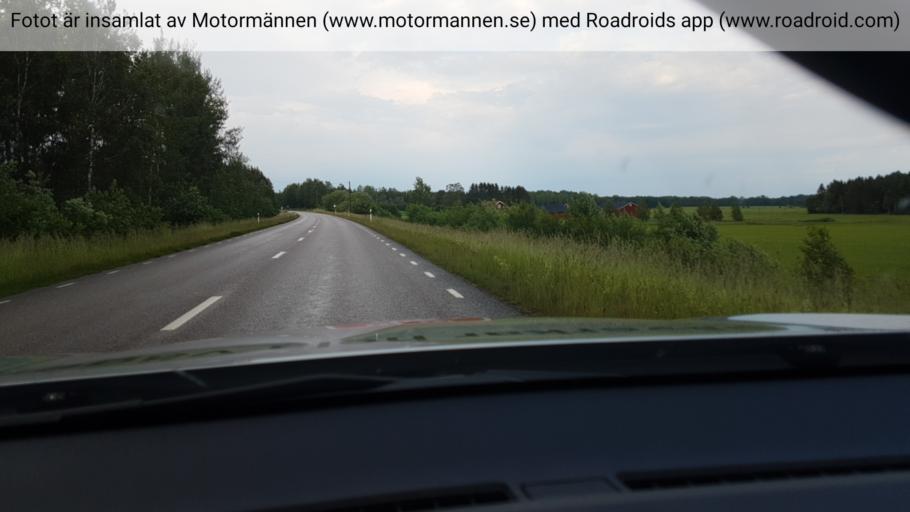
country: SE
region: Vaestra Goetaland
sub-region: Hjo Kommun
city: Hjo
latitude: 58.2393
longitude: 14.2264
